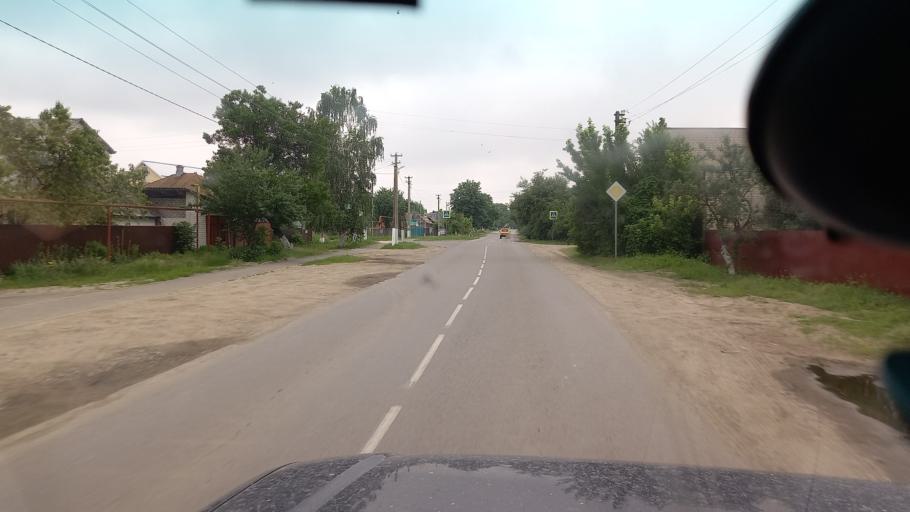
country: RU
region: Krasnodarskiy
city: Mostovskoy
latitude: 44.4146
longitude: 40.7814
